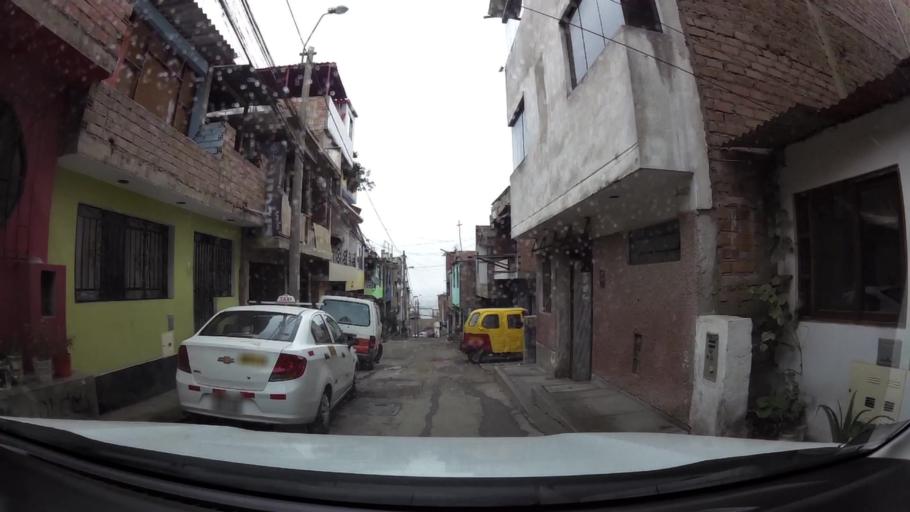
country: PE
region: Lima
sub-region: Lima
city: Surco
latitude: -12.1692
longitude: -76.9567
